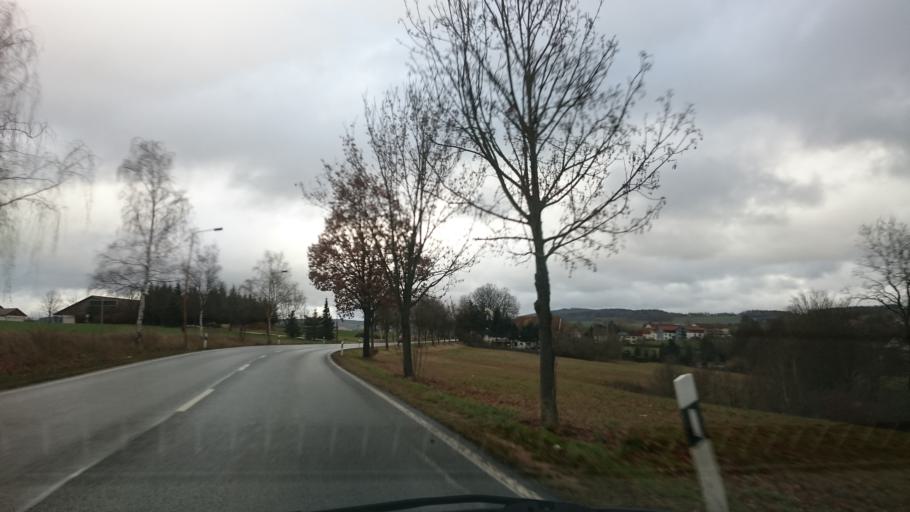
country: DE
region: Saxony
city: Kirchberg
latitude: 50.6552
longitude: 12.5572
